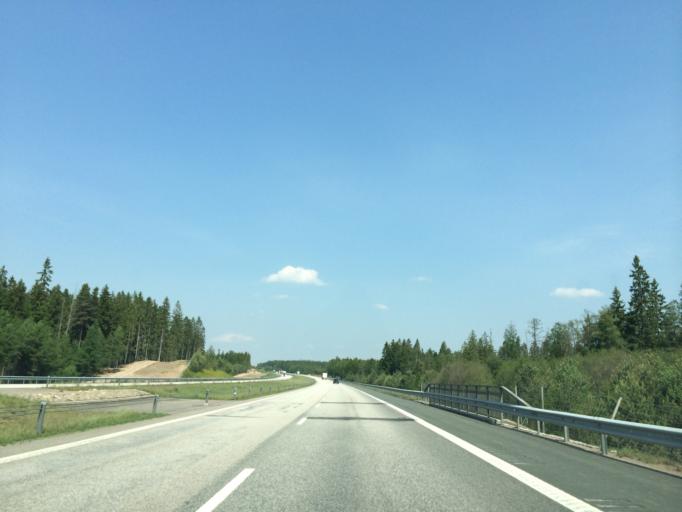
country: SE
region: Joenkoeping
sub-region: Varnamo Kommun
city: Varnamo
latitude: 57.0938
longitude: 14.0660
